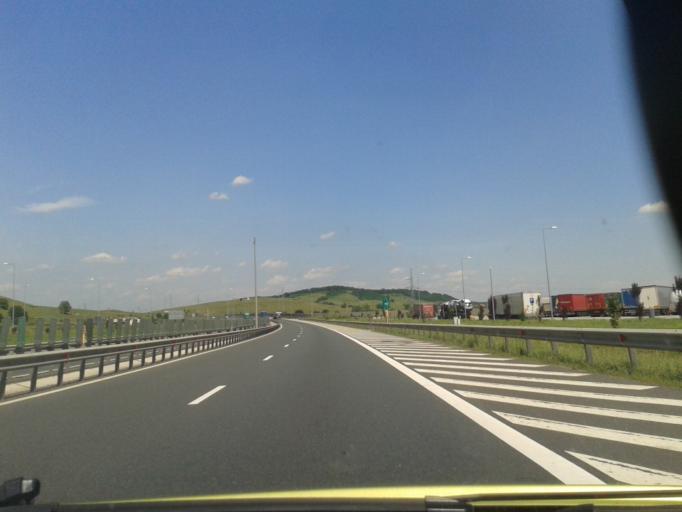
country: RO
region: Sibiu
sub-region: Comuna Cristian
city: Cristian
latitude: 45.7884
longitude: 24.0096
